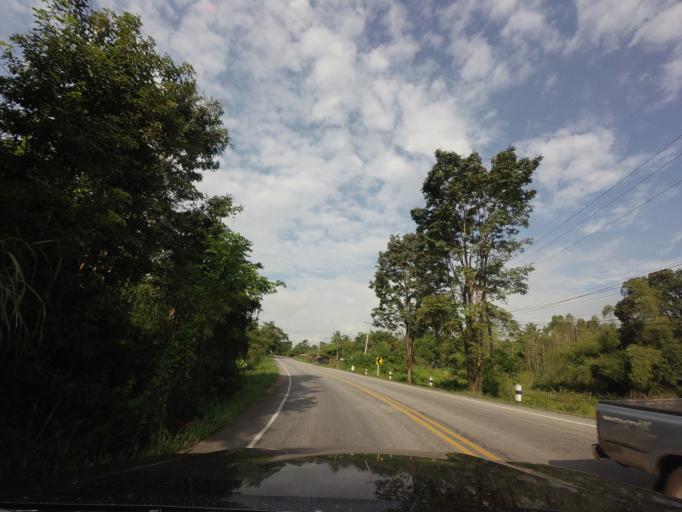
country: TH
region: Nong Khai
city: Pho Tak
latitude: 17.8076
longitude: 102.3300
